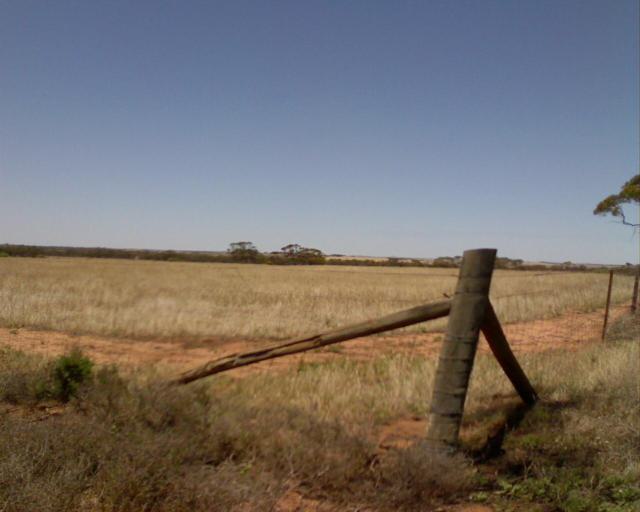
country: AU
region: South Australia
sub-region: Kimba
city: Caralue
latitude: -32.9455
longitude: 135.2801
